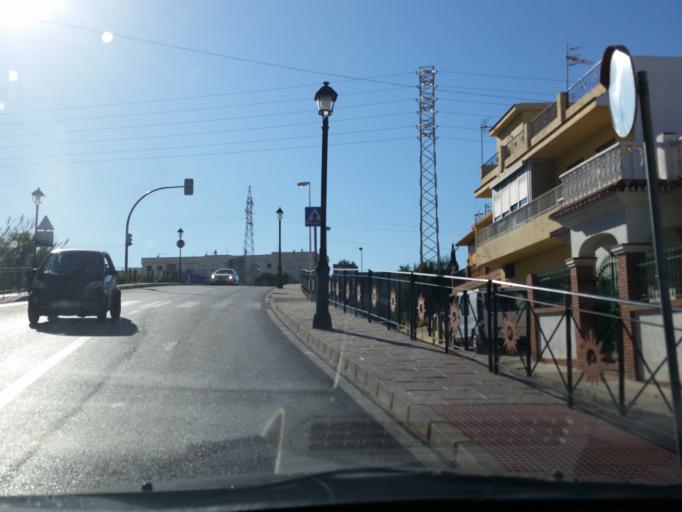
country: ES
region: Andalusia
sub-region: Provincia de Malaga
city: Fuengirola
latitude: 36.5573
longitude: -4.6179
